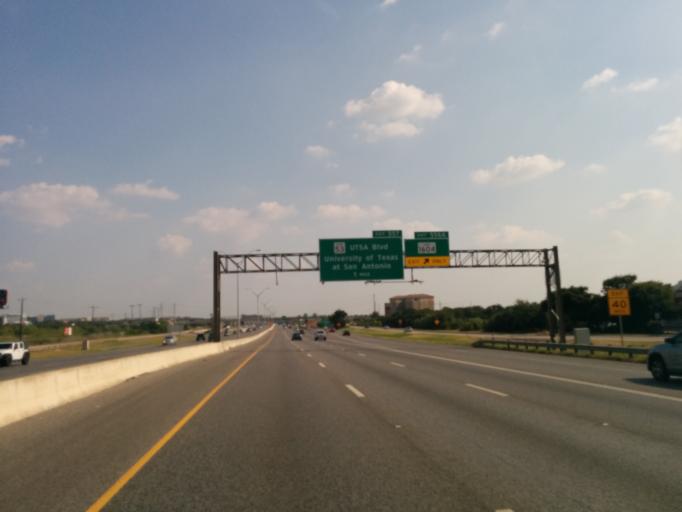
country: US
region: Texas
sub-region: Bexar County
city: Shavano Park
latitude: 29.5973
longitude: -98.5995
